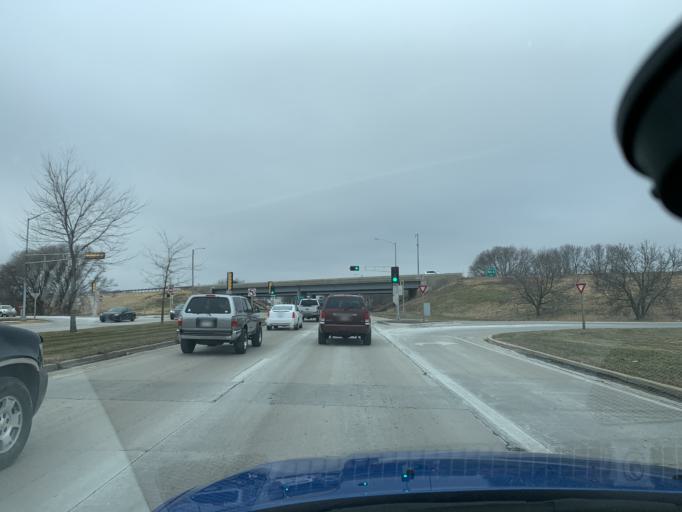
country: US
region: Wisconsin
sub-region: Dane County
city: Sun Prairie
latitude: 43.1875
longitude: -89.2316
